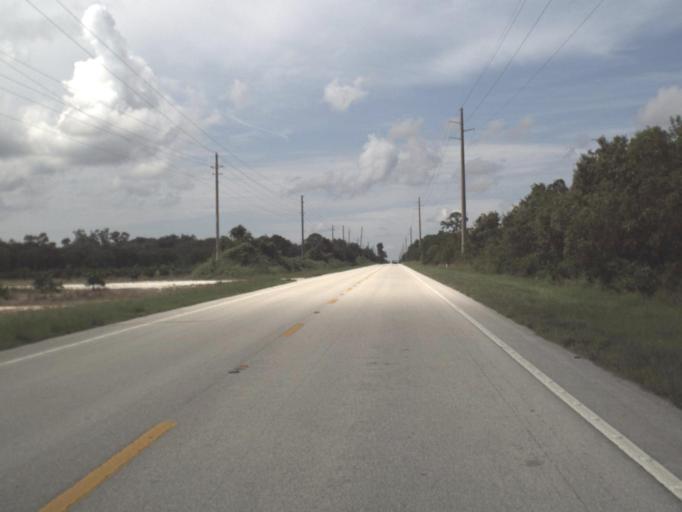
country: US
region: Florida
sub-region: Highlands County
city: Placid Lakes
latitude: 27.2086
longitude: -81.3741
